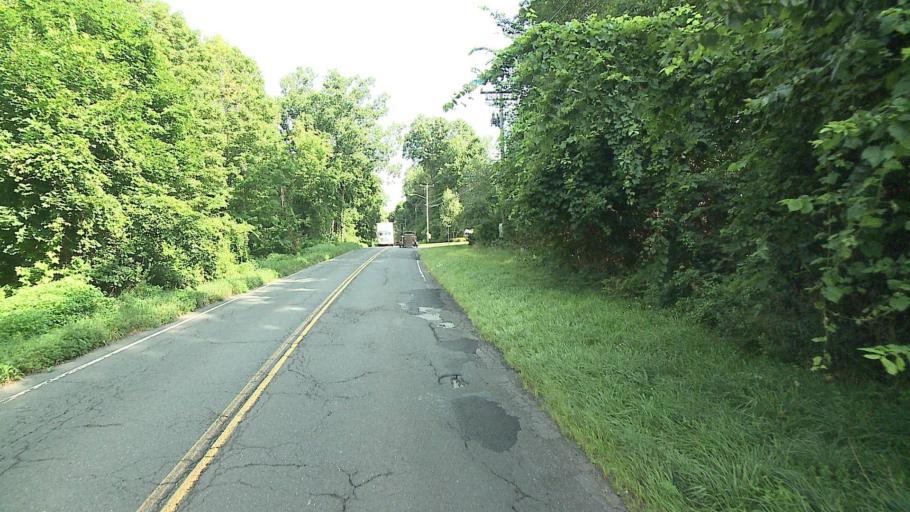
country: US
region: Connecticut
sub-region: Fairfield County
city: Danbury
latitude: 41.4540
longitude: -73.4758
